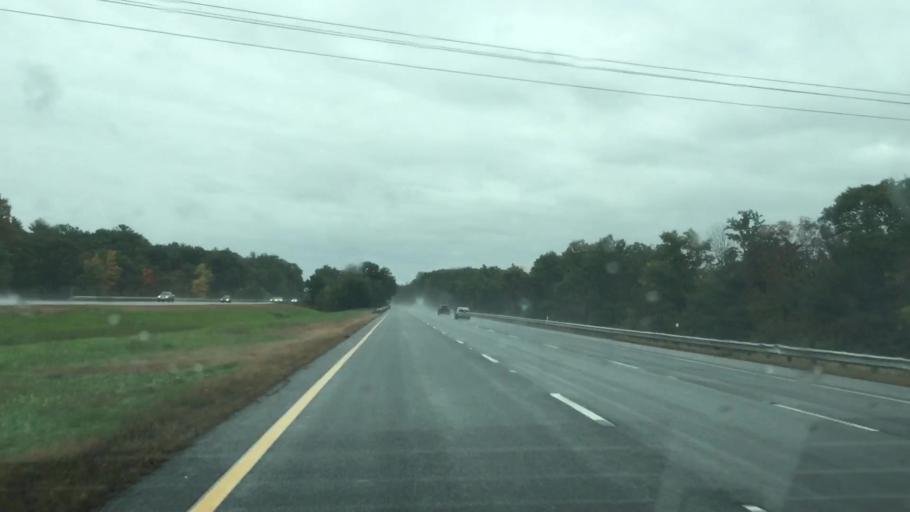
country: US
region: Massachusetts
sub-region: Essex County
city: Merrimac
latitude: 42.8342
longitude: -70.9699
